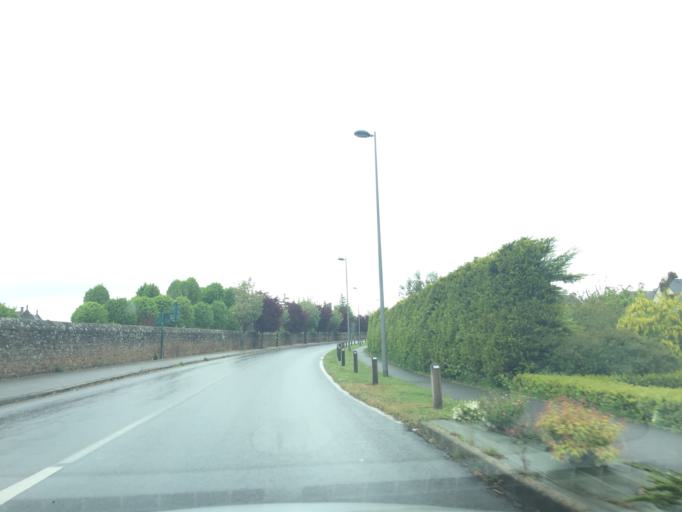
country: FR
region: Brittany
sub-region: Departement des Cotes-d'Armor
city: Crehen
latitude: 48.5434
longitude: -2.2126
